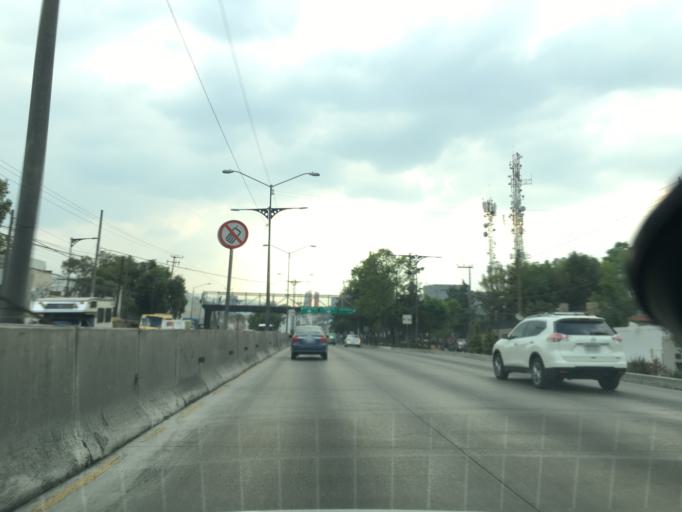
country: MX
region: Mexico City
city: Col. Bosques de las Lomas
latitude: 19.3792
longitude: -99.2574
